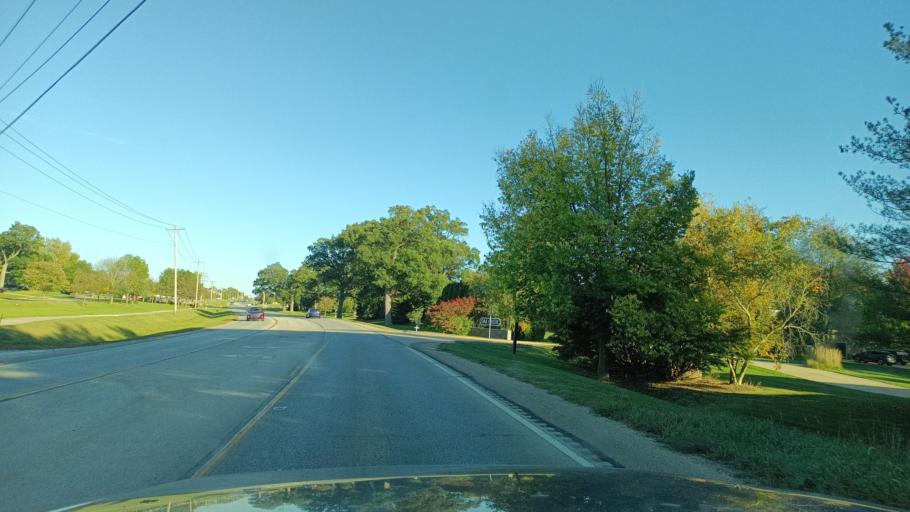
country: US
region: Illinois
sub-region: Champaign County
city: Mahomet
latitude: 40.1877
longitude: -88.3894
